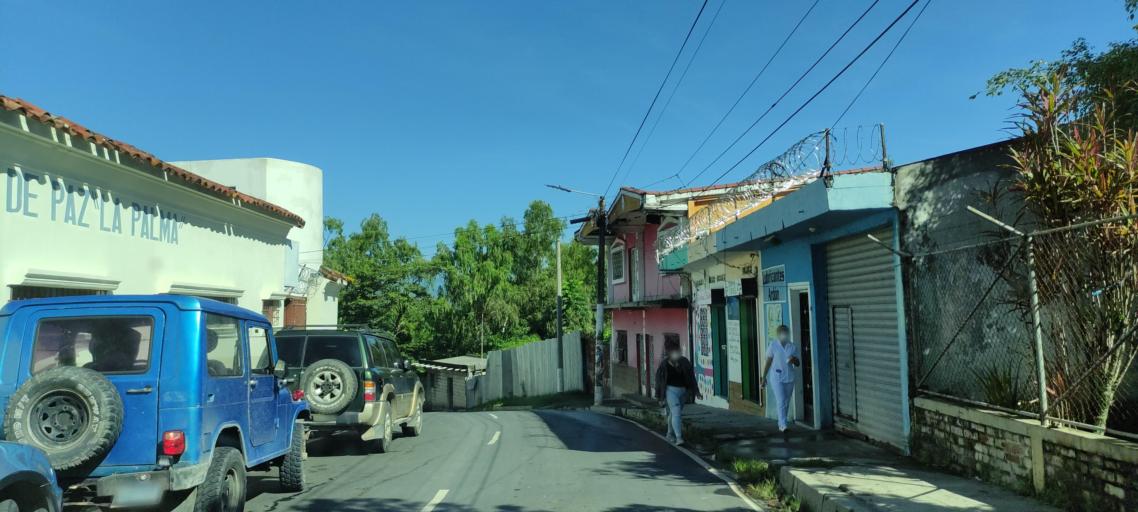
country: HN
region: Ocotepeque
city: Antigua Ocotepeque
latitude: 14.3177
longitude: -89.1706
